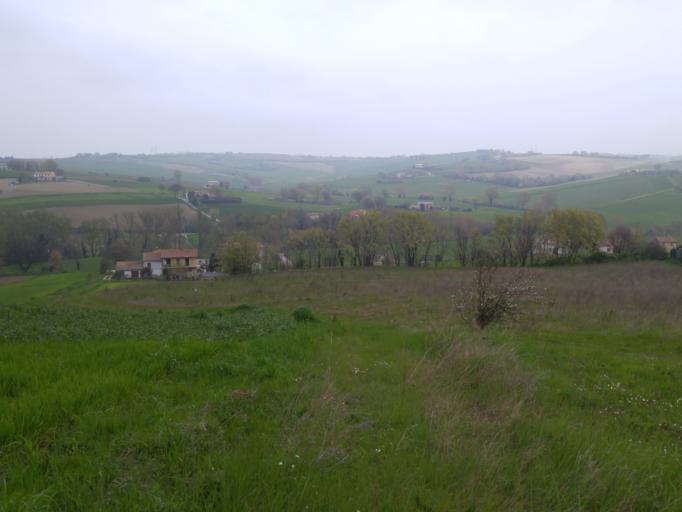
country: IT
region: The Marches
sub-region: Provincia di Pesaro e Urbino
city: Calcinelli
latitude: 43.7728
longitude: 12.9158
